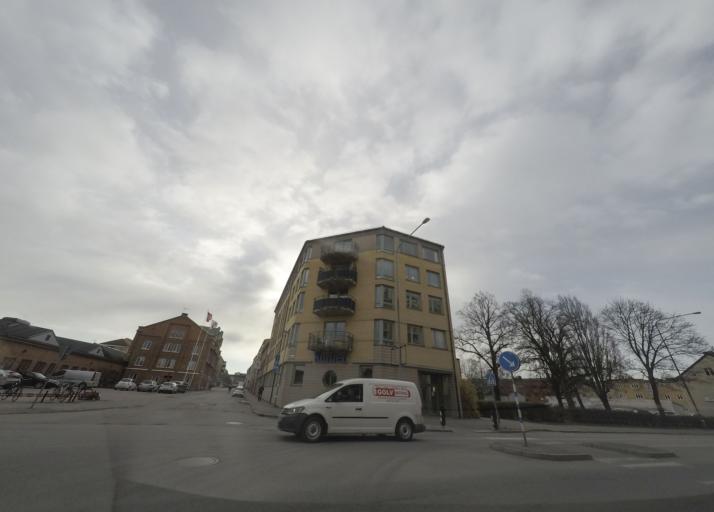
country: SE
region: Soedermanland
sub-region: Katrineholms Kommun
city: Katrineholm
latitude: 58.9960
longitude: 16.2010
